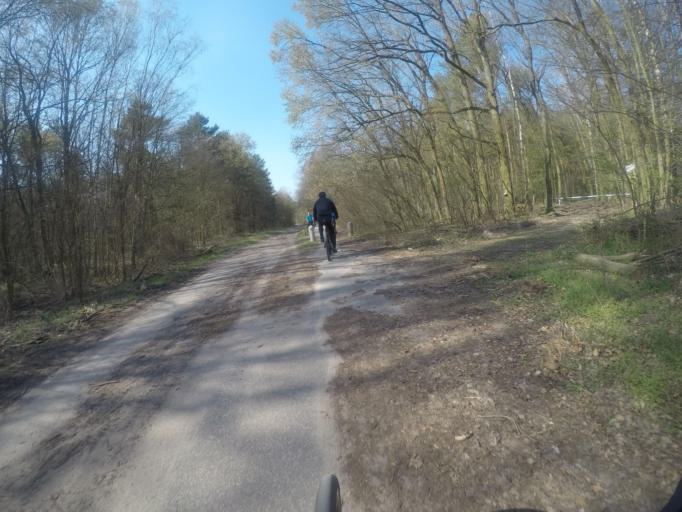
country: DE
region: Brandenburg
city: Hennigsdorf
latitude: 52.6410
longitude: 13.1691
